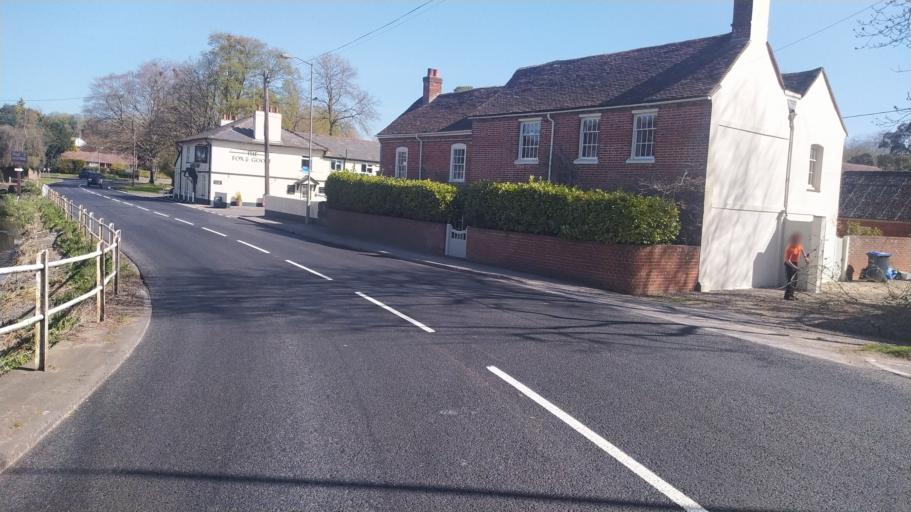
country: GB
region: England
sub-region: Wiltshire
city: Wilton
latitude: 51.0370
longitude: -1.8464
